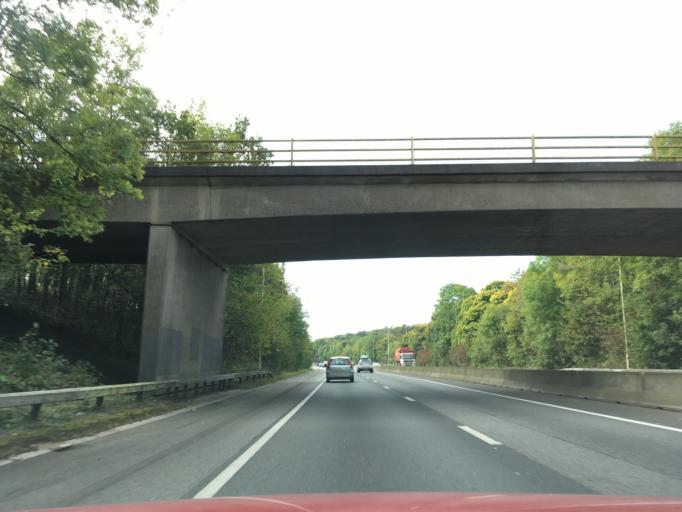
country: GB
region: Wales
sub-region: Cardiff
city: Cardiff
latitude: 51.5217
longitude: -3.1395
